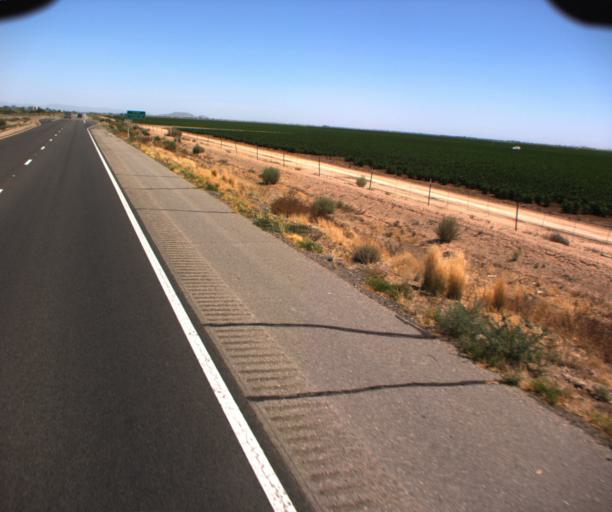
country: US
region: Arizona
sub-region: Pinal County
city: Maricopa
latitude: 32.9981
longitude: -112.0478
